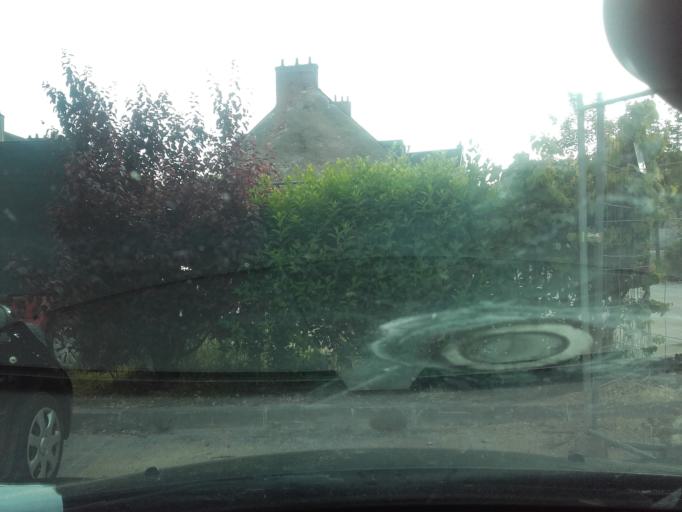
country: FR
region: Centre
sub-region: Departement du Loir-et-Cher
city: Chouzy-sur-Cisse
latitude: 47.5224
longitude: 1.2462
